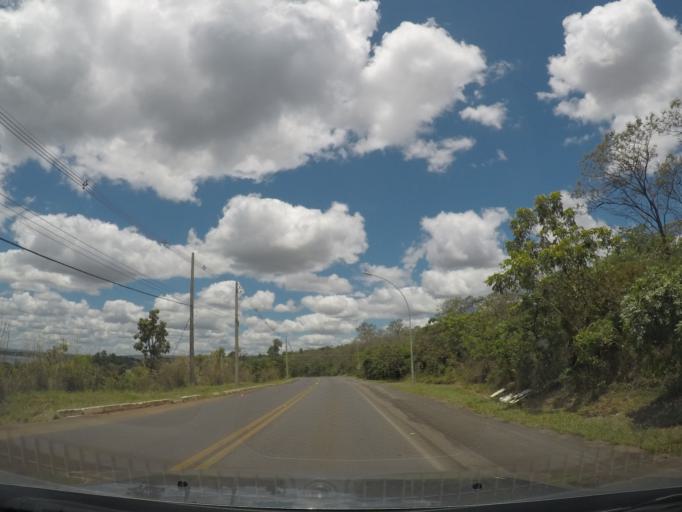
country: BR
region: Federal District
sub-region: Brasilia
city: Brasilia
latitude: -15.7857
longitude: -47.8050
